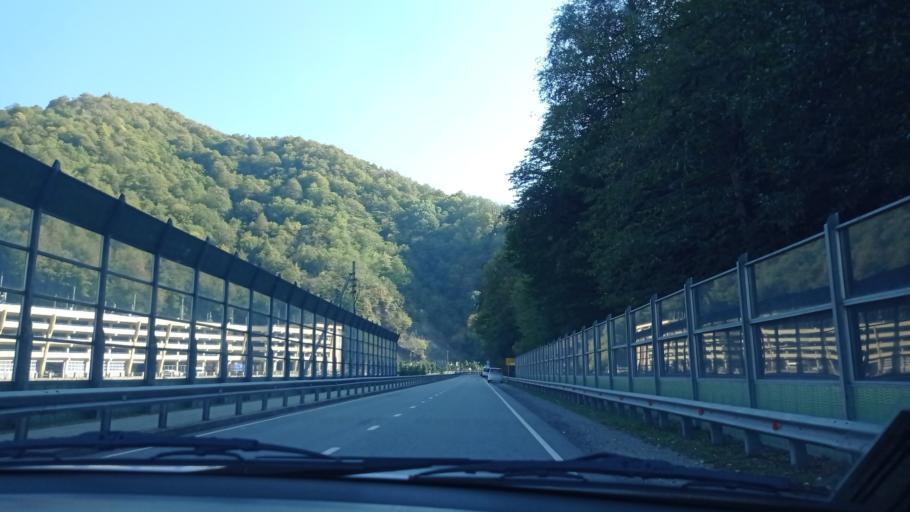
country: RU
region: Krasnodarskiy
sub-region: Sochi City
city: Krasnaya Polyana
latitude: 43.6850
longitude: 40.2771
